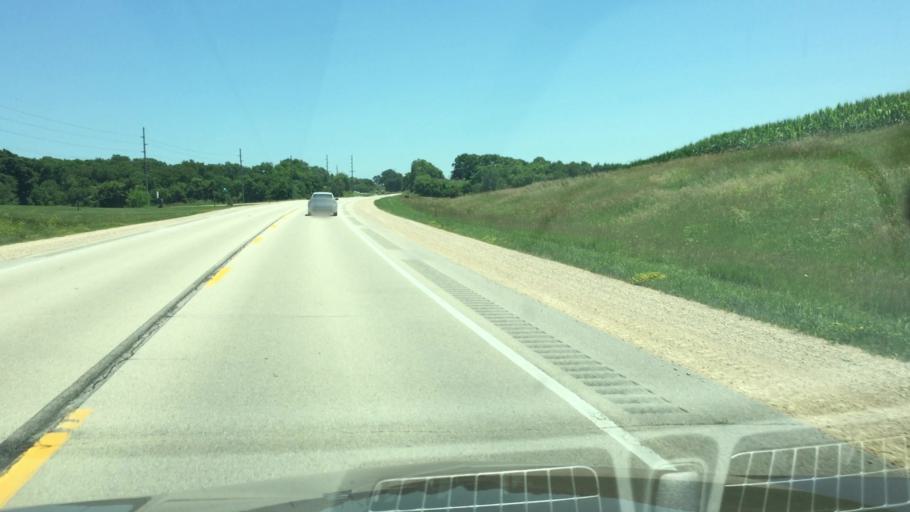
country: US
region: Iowa
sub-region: Jackson County
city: Maquoketa
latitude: 42.0640
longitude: -90.7634
